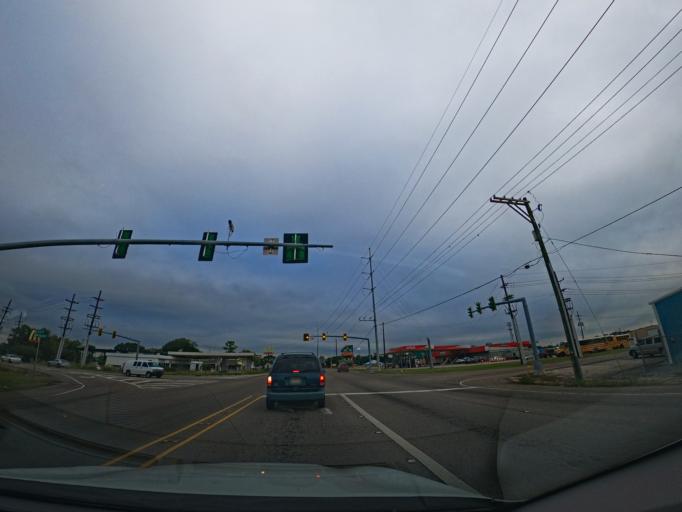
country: US
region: Louisiana
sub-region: Terrebonne Parish
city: Presquille
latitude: 29.5704
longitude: -90.6829
